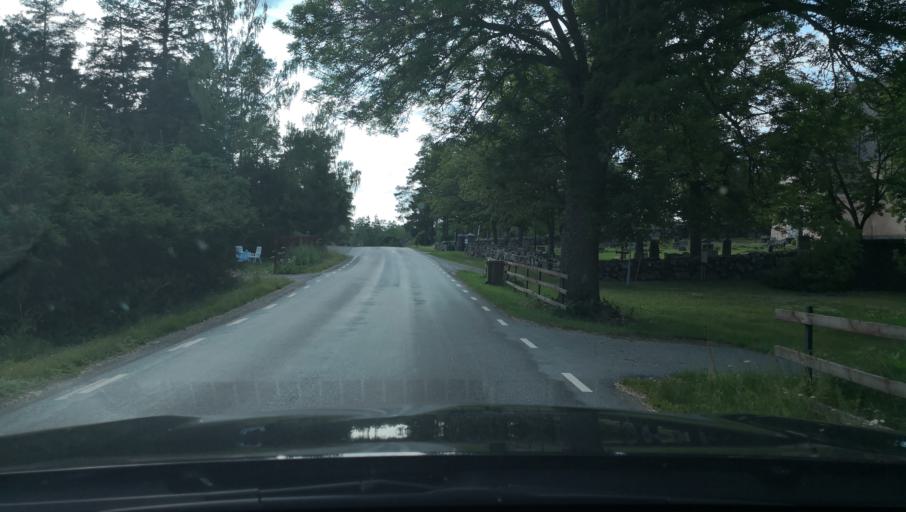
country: SE
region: Uppsala
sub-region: Enkopings Kommun
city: Orsundsbro
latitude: 59.6881
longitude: 17.3860
